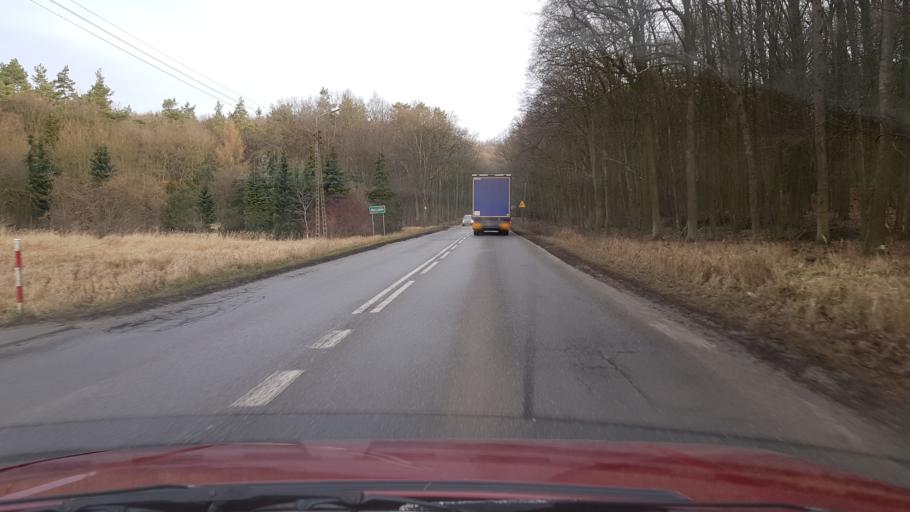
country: PL
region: West Pomeranian Voivodeship
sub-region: Powiat policki
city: Police
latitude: 53.5213
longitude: 14.5685
